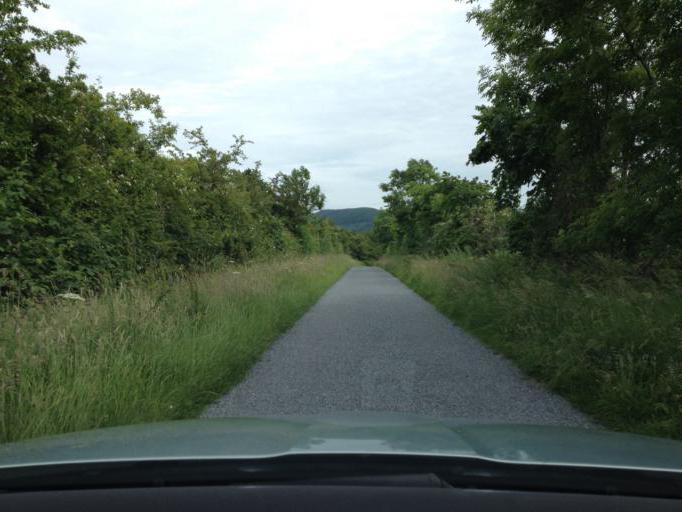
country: GB
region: Scotland
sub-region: Perth and Kinross
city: Bridge of Earn
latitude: 56.3274
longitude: -3.4021
